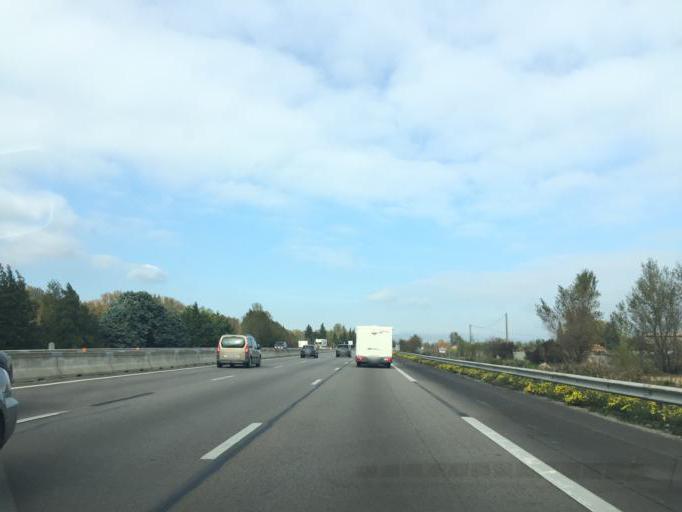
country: FR
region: Rhone-Alpes
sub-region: Departement de la Drome
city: Saulce-sur-Rhone
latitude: 44.6895
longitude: 4.7923
